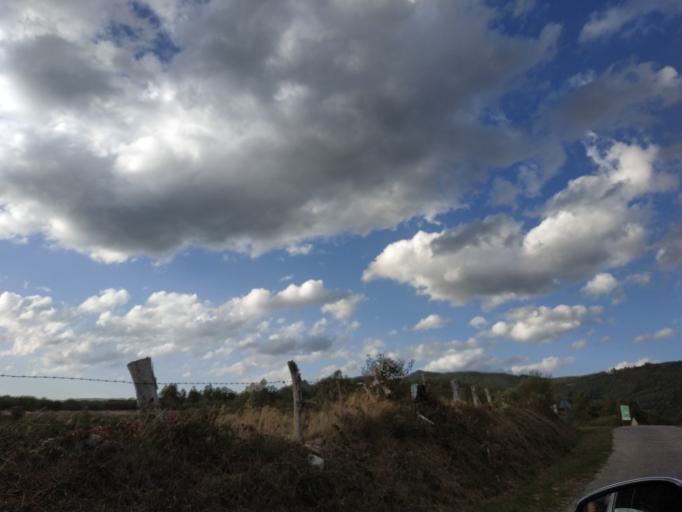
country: ES
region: Castille and Leon
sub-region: Provincia de Leon
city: Candin
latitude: 42.8609
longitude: -6.8645
